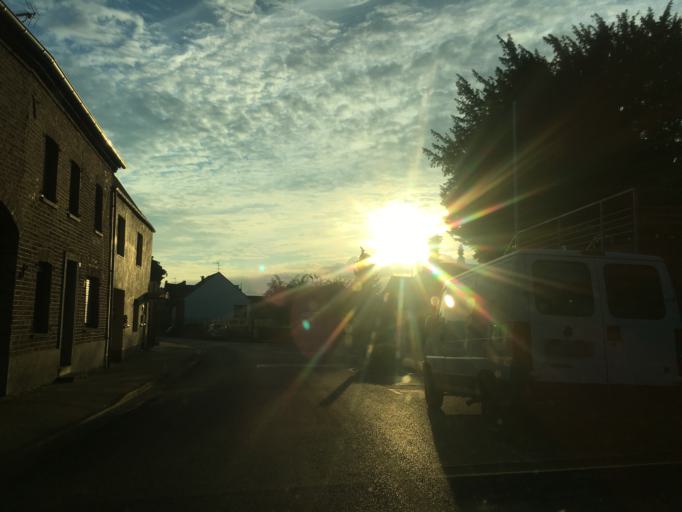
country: DE
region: North Rhine-Westphalia
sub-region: Regierungsbezirk Koln
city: Linnich
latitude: 50.9997
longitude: 6.2816
